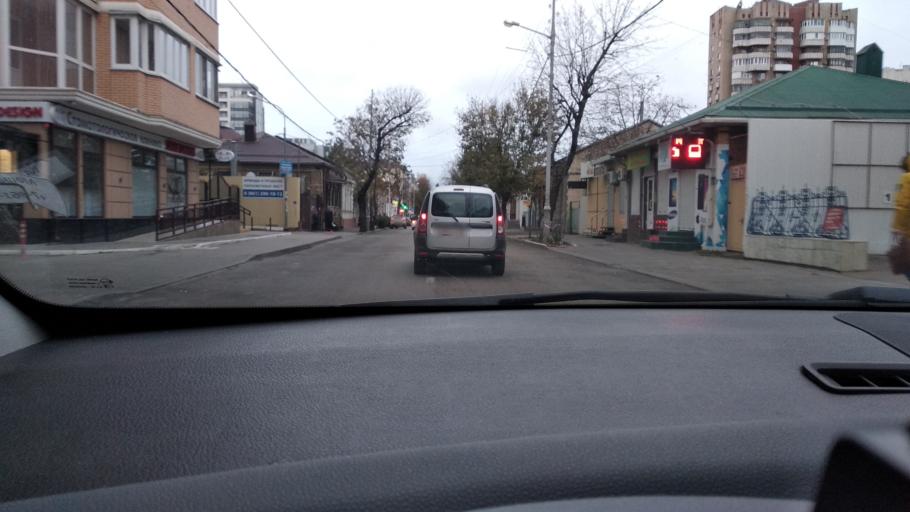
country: RU
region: Krasnodarskiy
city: Krasnodar
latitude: 45.0229
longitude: 38.9761
